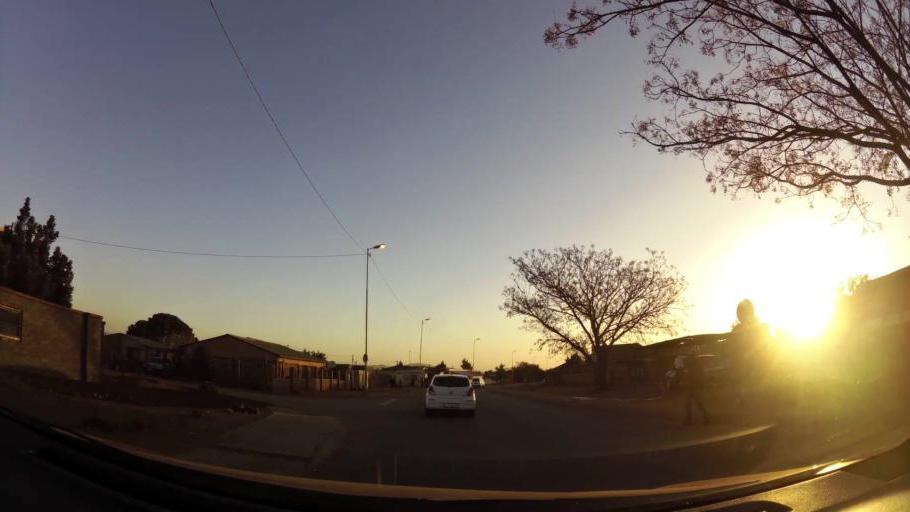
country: ZA
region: Gauteng
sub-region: City of Tshwane Metropolitan Municipality
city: Mabopane
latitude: -25.5815
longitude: 28.0868
